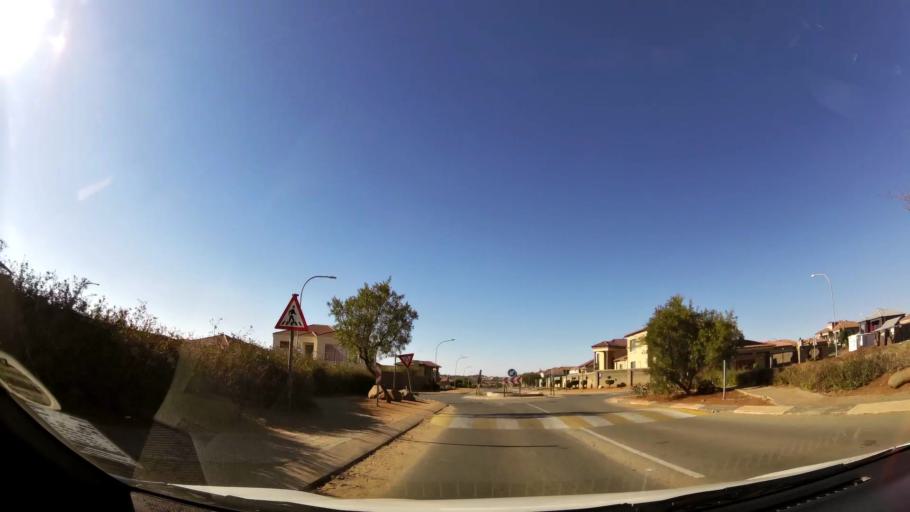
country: ZA
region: Limpopo
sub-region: Capricorn District Municipality
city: Polokwane
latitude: -23.9101
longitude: 29.5040
